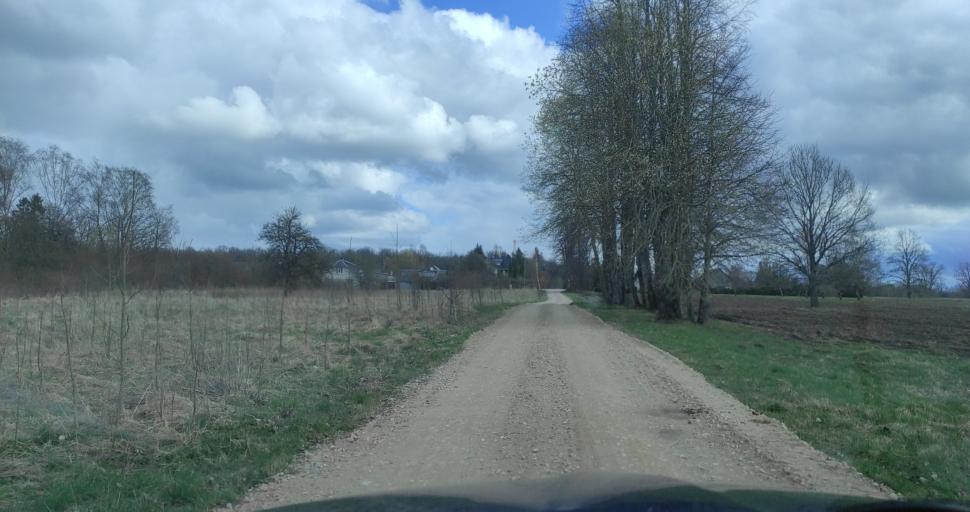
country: LV
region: Aizpute
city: Aizpute
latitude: 56.7160
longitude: 21.5877
